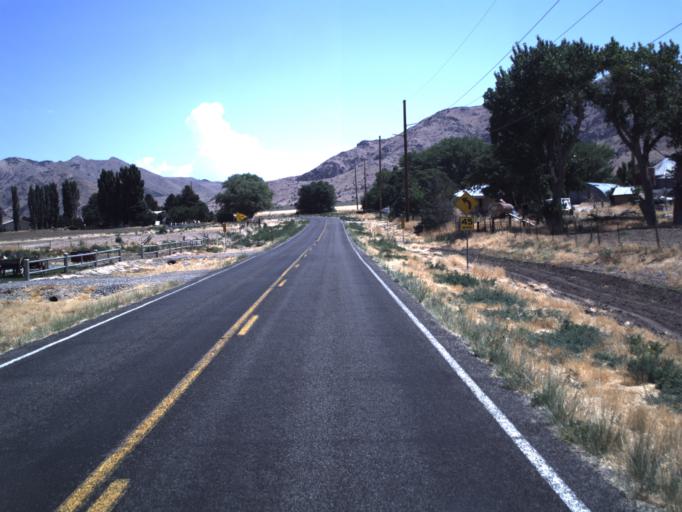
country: US
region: Utah
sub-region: Millard County
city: Delta
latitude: 39.4700
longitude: -112.2724
